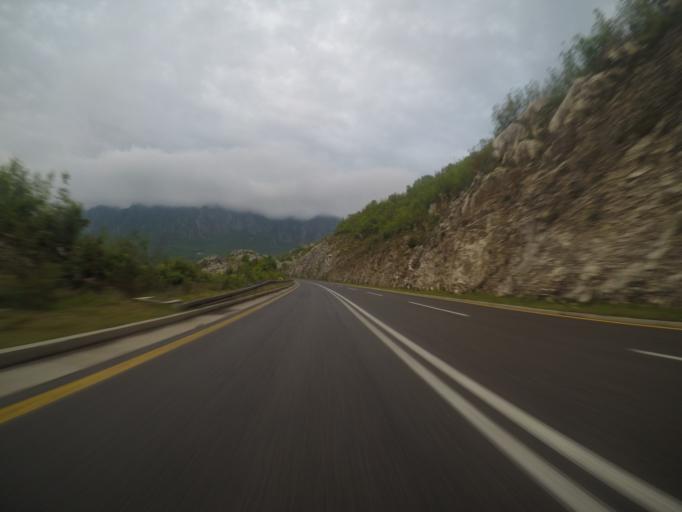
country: ME
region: Bar
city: Sutomore
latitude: 42.2125
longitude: 19.0480
